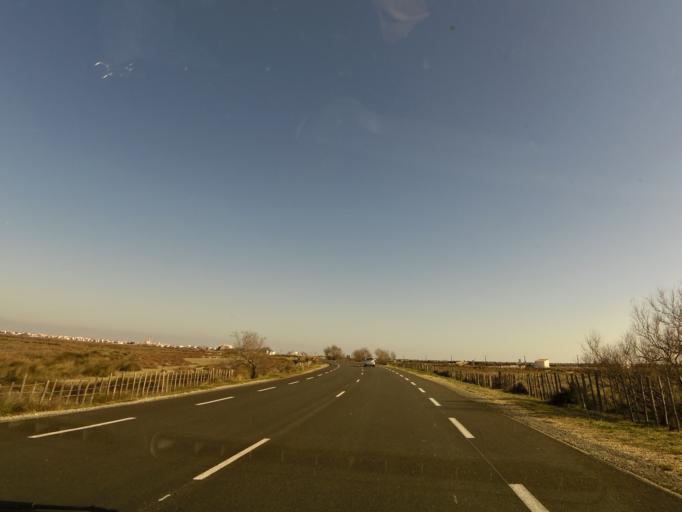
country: FR
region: Provence-Alpes-Cote d'Azur
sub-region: Departement des Bouches-du-Rhone
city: Saintes-Maries-de-la-Mer
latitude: 43.4510
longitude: 4.4044
